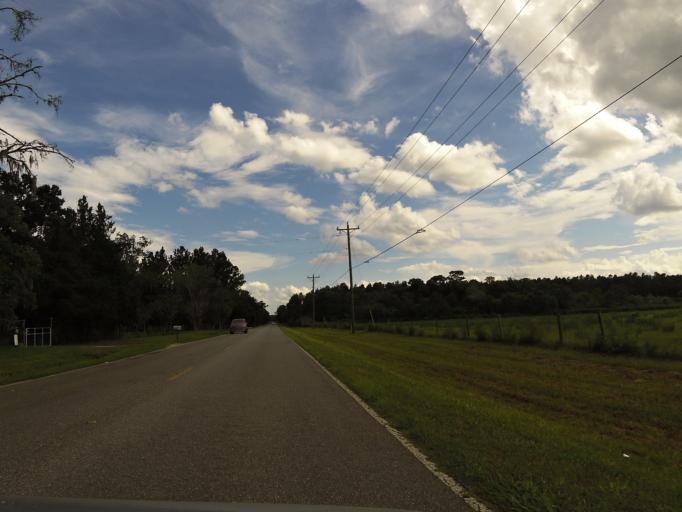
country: US
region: Florida
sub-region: Clay County
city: Green Cove Springs
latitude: 30.0008
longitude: -81.7315
